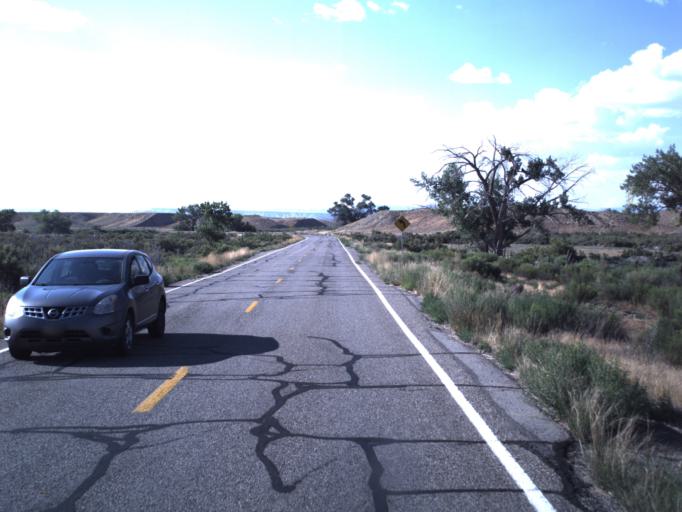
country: US
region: Utah
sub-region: Emery County
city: Huntington
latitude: 39.4287
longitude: -110.8621
